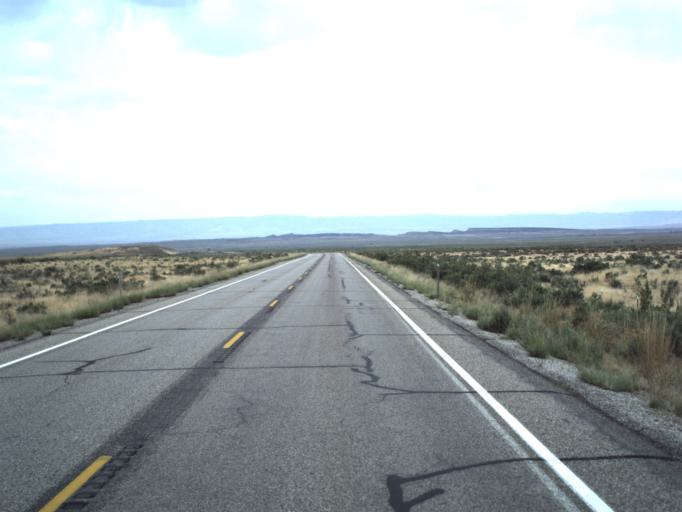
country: US
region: Utah
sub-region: Carbon County
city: East Carbon City
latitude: 39.5360
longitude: -110.4947
